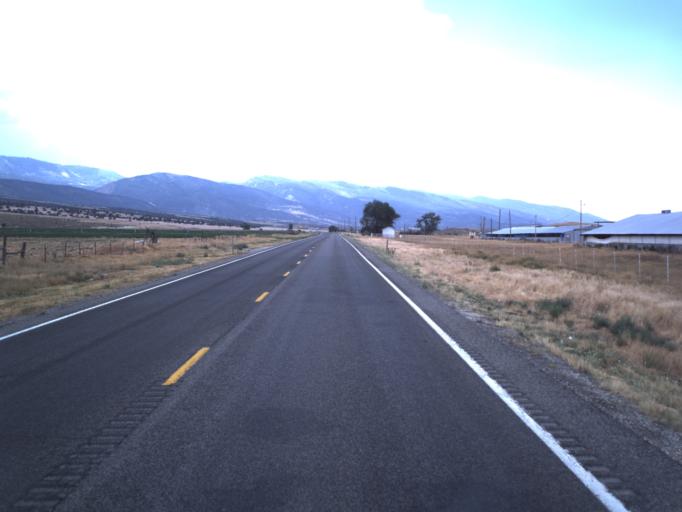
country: US
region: Utah
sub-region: Sanpete County
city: Ephraim
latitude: 39.4293
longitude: -111.5623
